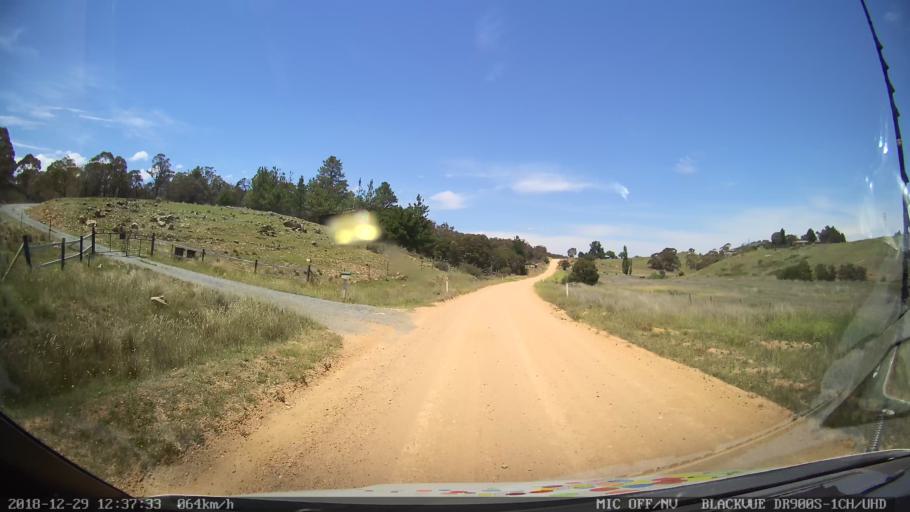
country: AU
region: Australian Capital Territory
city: Macarthur
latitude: -35.5812
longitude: 149.2285
